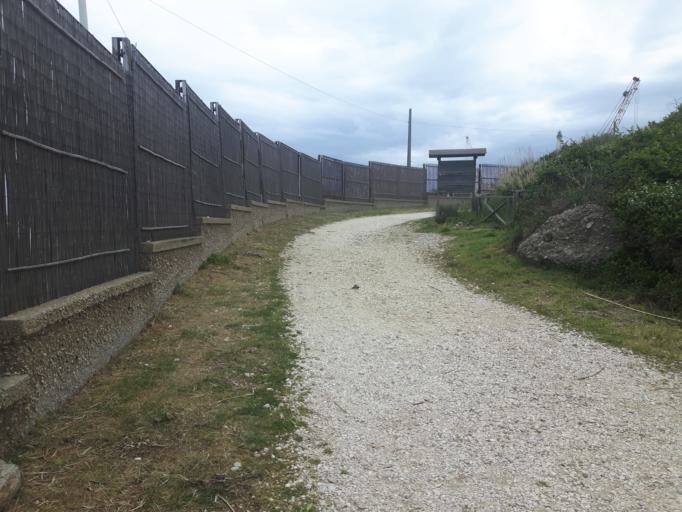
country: IT
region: Abruzzo
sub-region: Provincia di Chieti
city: Vasto
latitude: 42.1734
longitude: 14.7087
